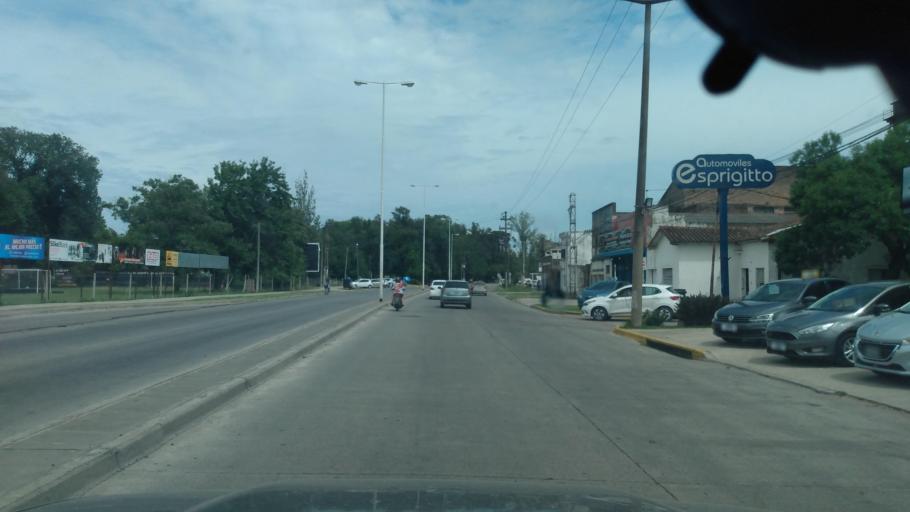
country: AR
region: Buenos Aires
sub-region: Partido de Lujan
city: Lujan
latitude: -34.5599
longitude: -59.1108
